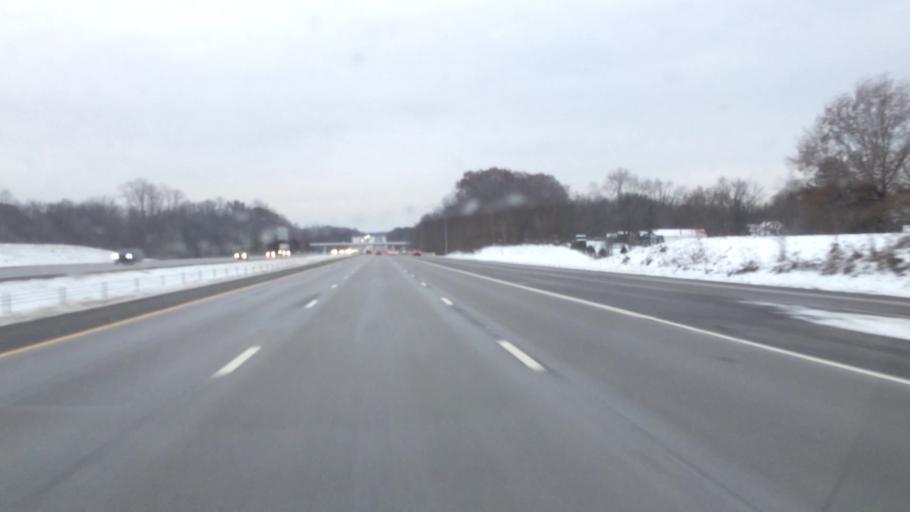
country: US
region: Ohio
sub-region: Medina County
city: Brunswick
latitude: 41.1911
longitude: -81.7906
